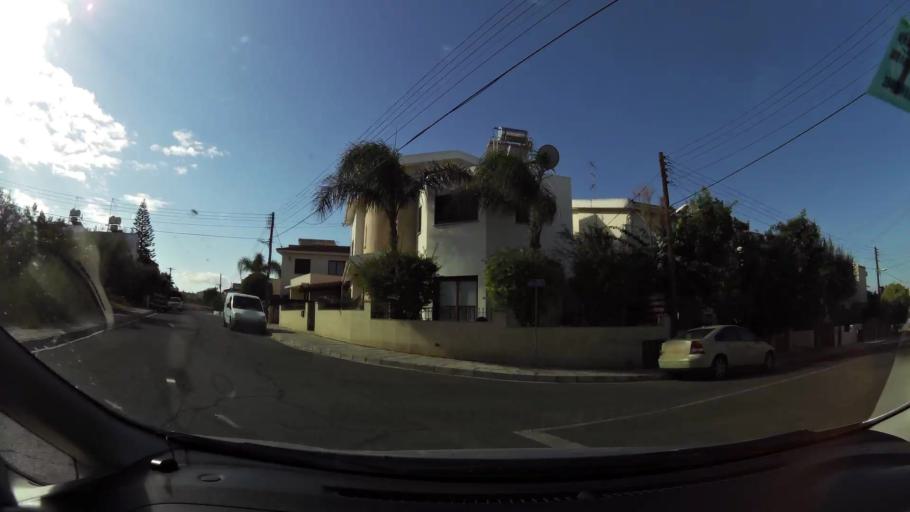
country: CY
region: Lefkosia
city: Nicosia
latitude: 35.1327
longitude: 33.3467
